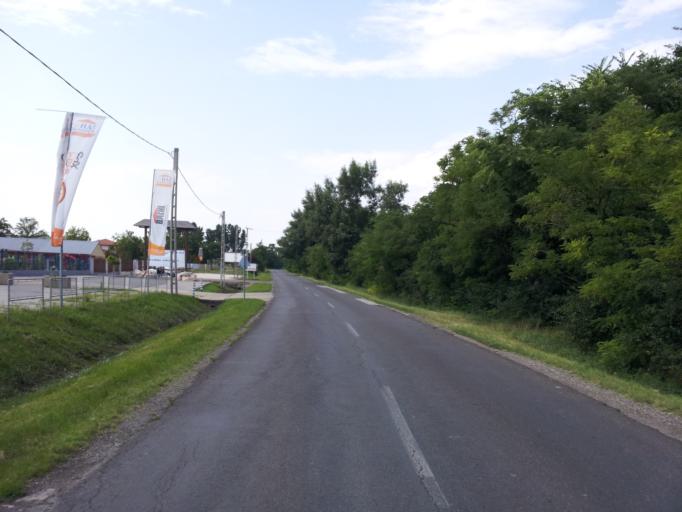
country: HU
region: Pest
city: Toekoel
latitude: 47.2956
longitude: 18.9800
